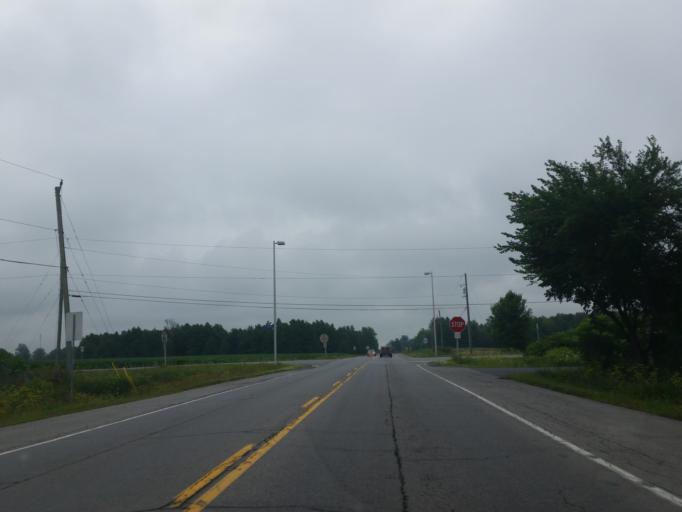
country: CA
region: Ontario
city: Clarence-Rockland
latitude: 45.3465
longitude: -75.3662
